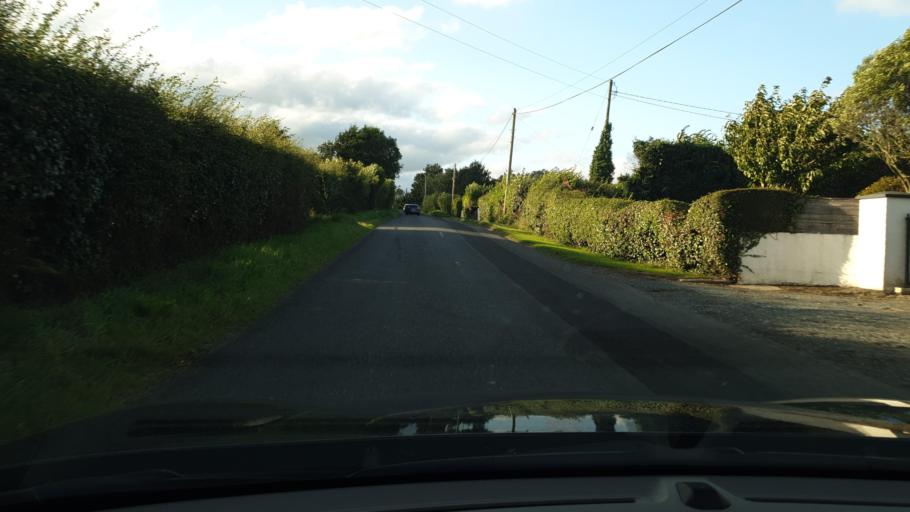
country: IE
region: Leinster
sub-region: Lu
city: Drogheda
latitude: 53.6747
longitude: -6.3263
